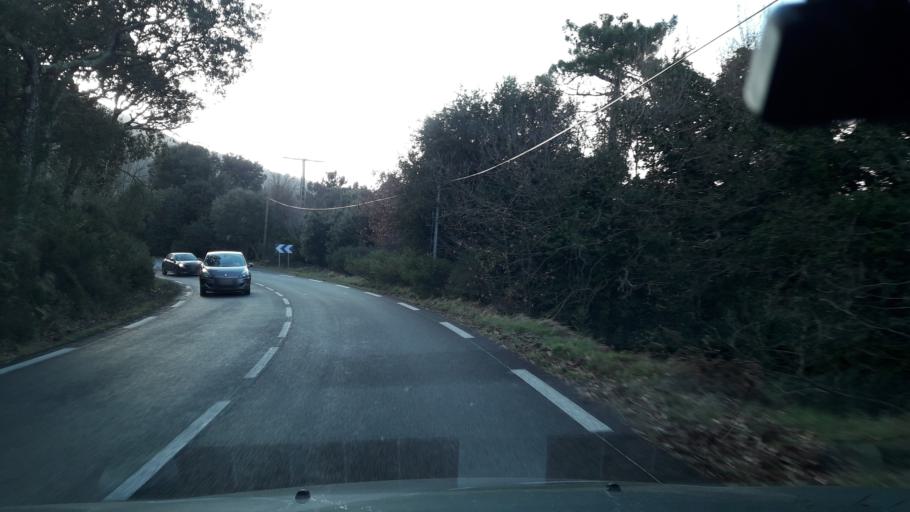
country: FR
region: Provence-Alpes-Cote d'Azur
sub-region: Departement du Var
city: Tanneron
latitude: 43.5166
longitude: 6.8335
